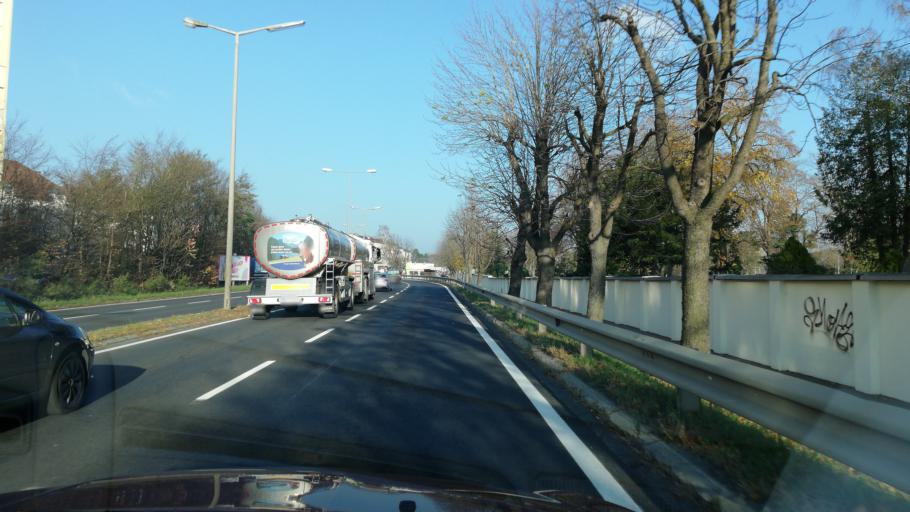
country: AT
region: Upper Austria
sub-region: Wels Stadt
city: Wels
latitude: 48.1725
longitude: 14.0317
